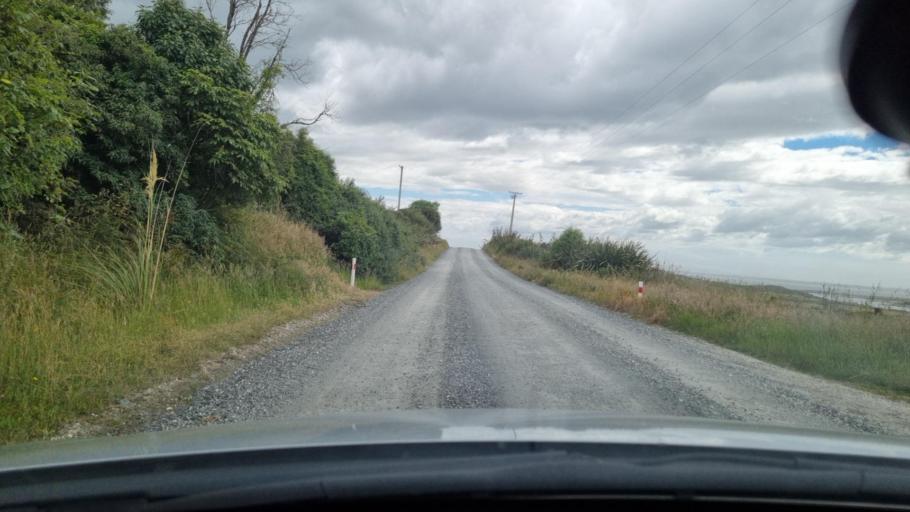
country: NZ
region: Southland
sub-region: Invercargill City
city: Bluff
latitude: -46.5266
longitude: 168.2699
